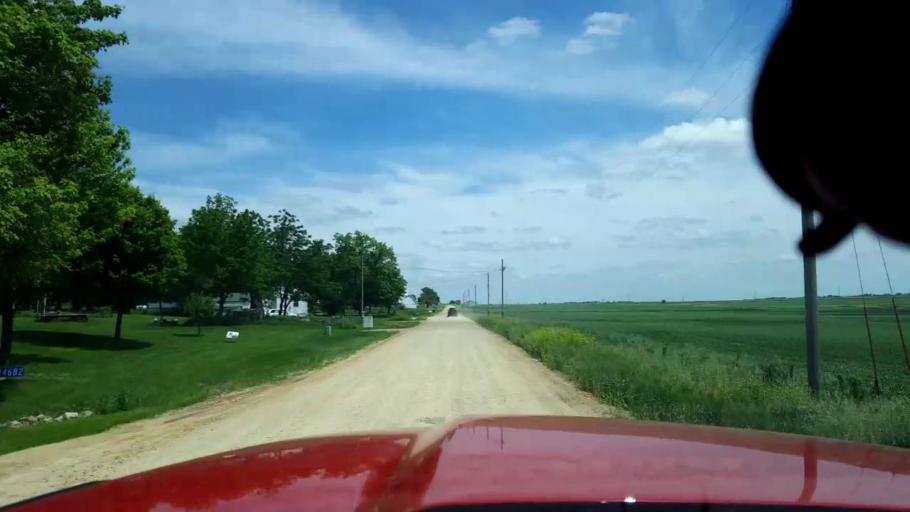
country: US
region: Iowa
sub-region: Linn County
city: Lisbon
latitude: 41.9538
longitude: -91.3592
